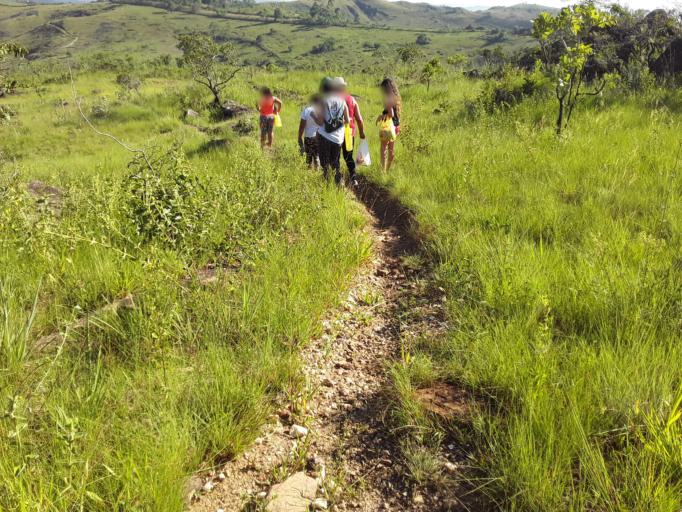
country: BR
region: Minas Gerais
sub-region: Sao Joao Del Rei
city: Sao Joao del Rei
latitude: -21.1275
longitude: -44.2755
